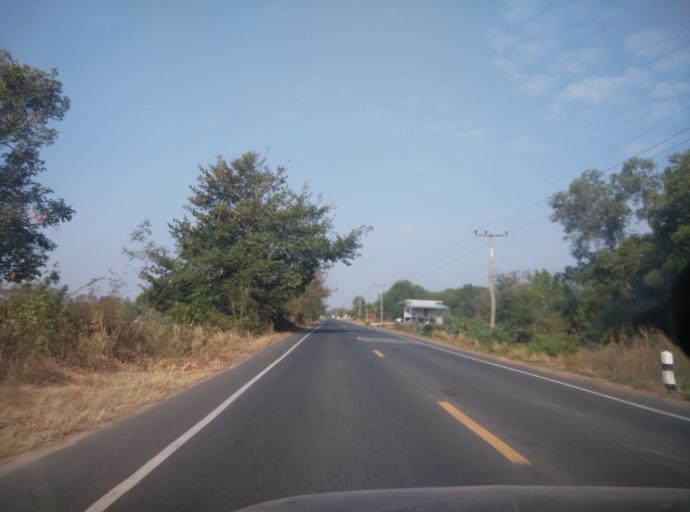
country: TH
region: Sisaket
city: Si Sa Ket
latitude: 15.1143
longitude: 104.2656
